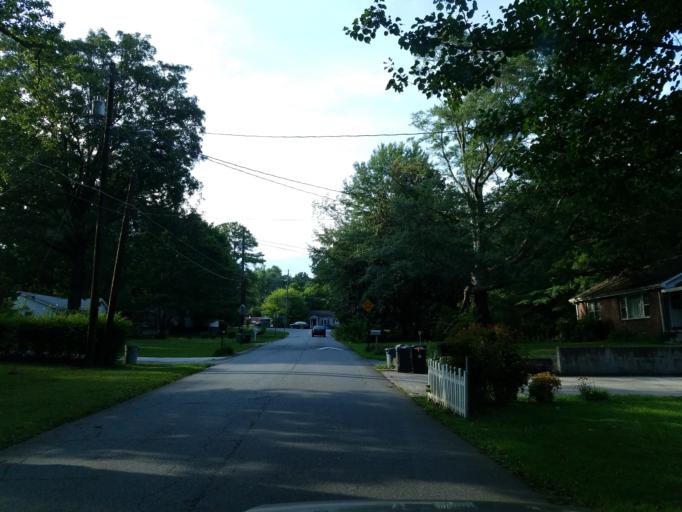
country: US
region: Georgia
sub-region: Cobb County
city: Marietta
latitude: 33.9355
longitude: -84.5492
